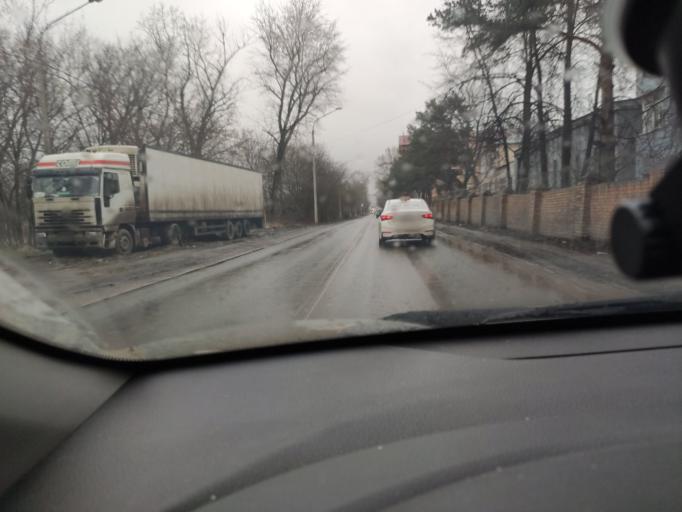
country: RU
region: Moskovskaya
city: Biryulevo Zapadnoye
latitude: 55.5654
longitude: 37.6460
